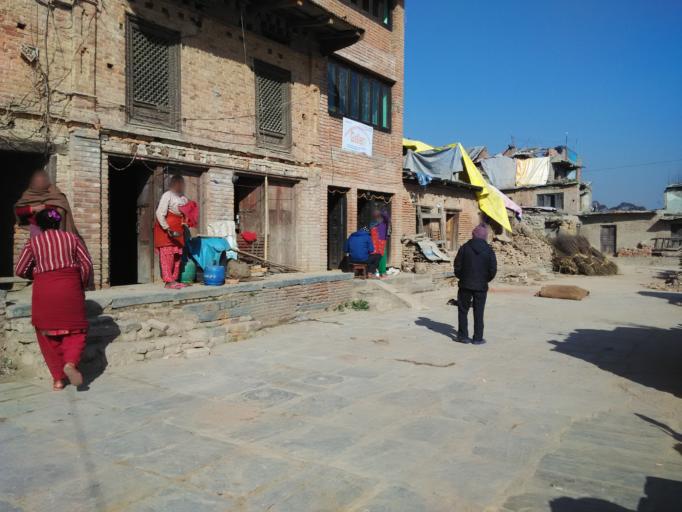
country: NP
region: Central Region
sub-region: Bagmati Zone
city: Patan
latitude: 27.6296
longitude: 85.3017
